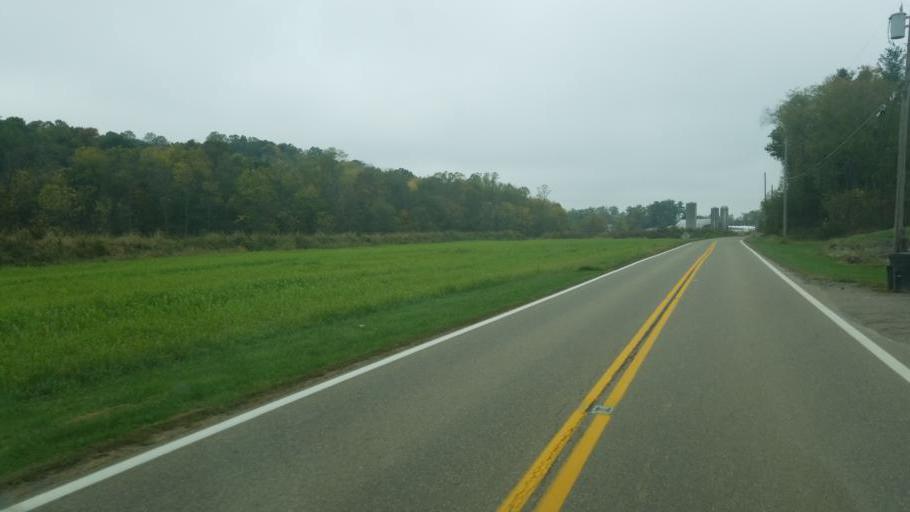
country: US
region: Ohio
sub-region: Tuscarawas County
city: Strasburg
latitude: 40.6554
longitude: -81.4930
